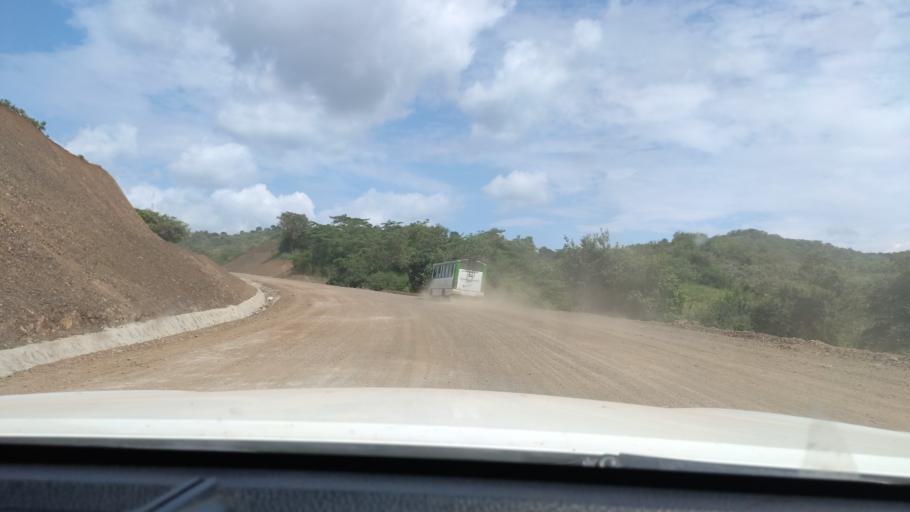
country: ET
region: Southern Nations, Nationalities, and People's Region
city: Felege Neway
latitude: 6.3902
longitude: 37.0626
